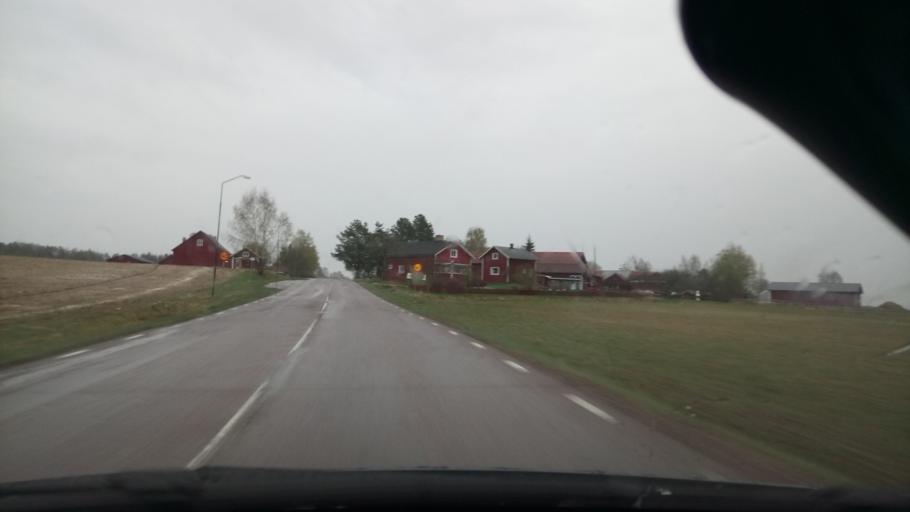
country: SE
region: Dalarna
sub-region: Borlange Kommun
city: Borlaenge
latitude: 60.4571
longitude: 15.4059
